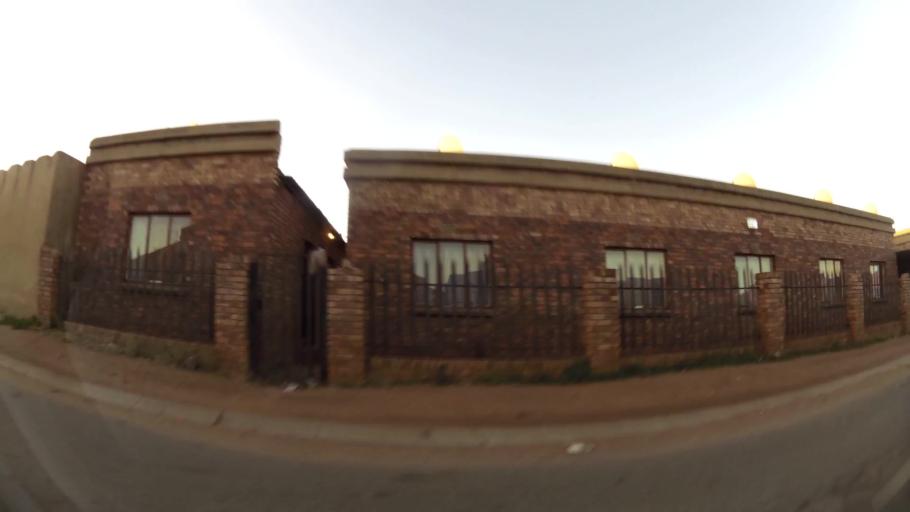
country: ZA
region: Gauteng
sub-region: Ekurhuleni Metropolitan Municipality
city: Tembisa
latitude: -25.9929
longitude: 28.2255
